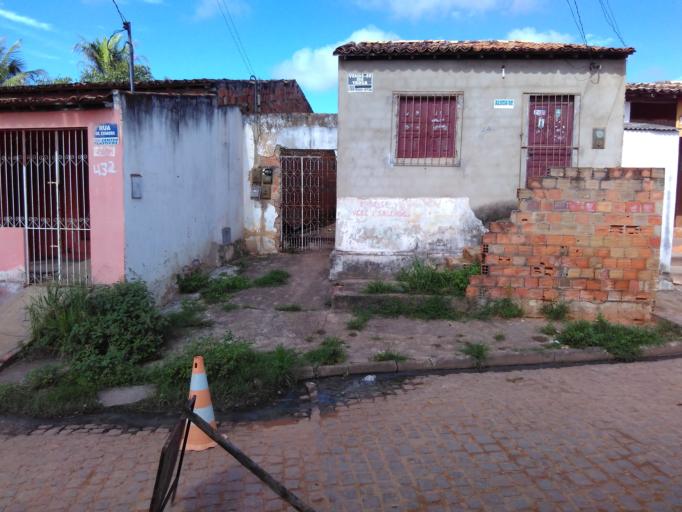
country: BR
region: Sergipe
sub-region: Lagarto
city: Lagarto
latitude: -10.9135
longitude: -37.6868
